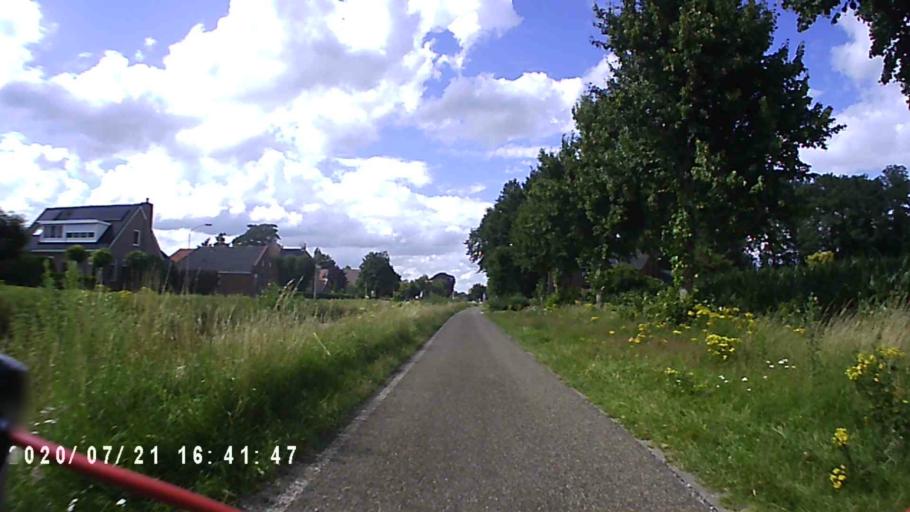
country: NL
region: Groningen
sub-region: Gemeente Hoogezand-Sappemeer
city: Sappemeer
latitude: 53.1018
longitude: 6.7875
